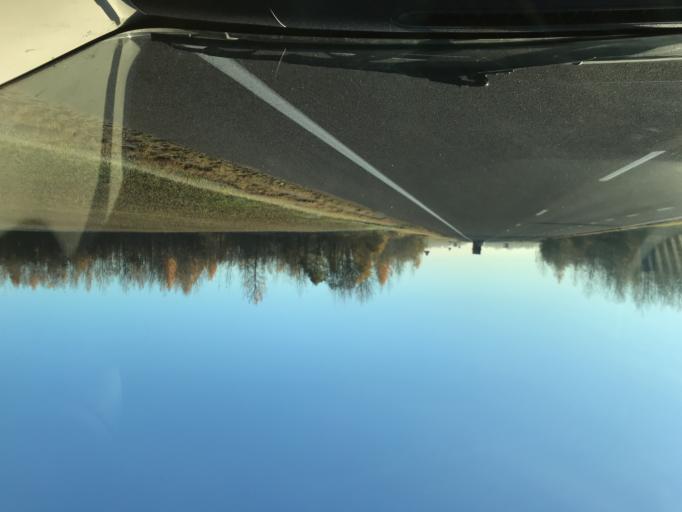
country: BY
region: Vitebsk
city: Vitebsk
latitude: 55.0030
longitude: 30.3355
